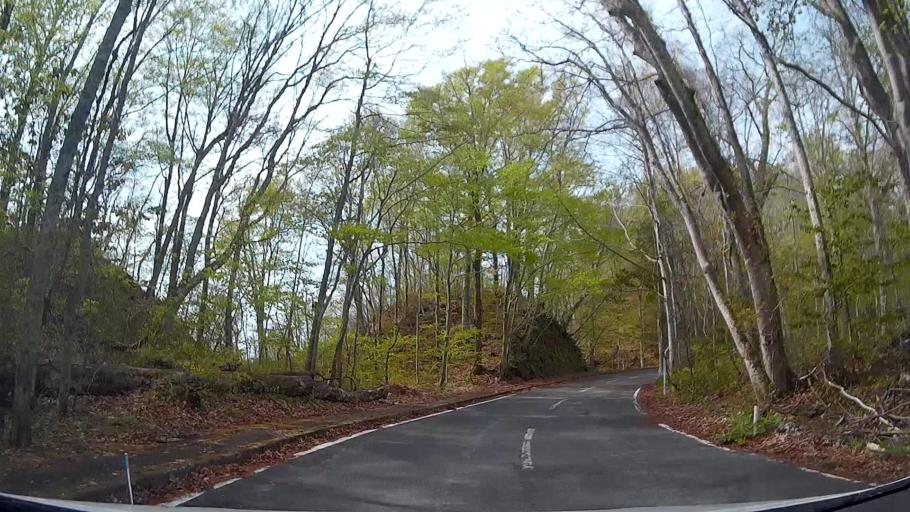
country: JP
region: Akita
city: Hanawa
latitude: 40.4365
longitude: 140.9165
